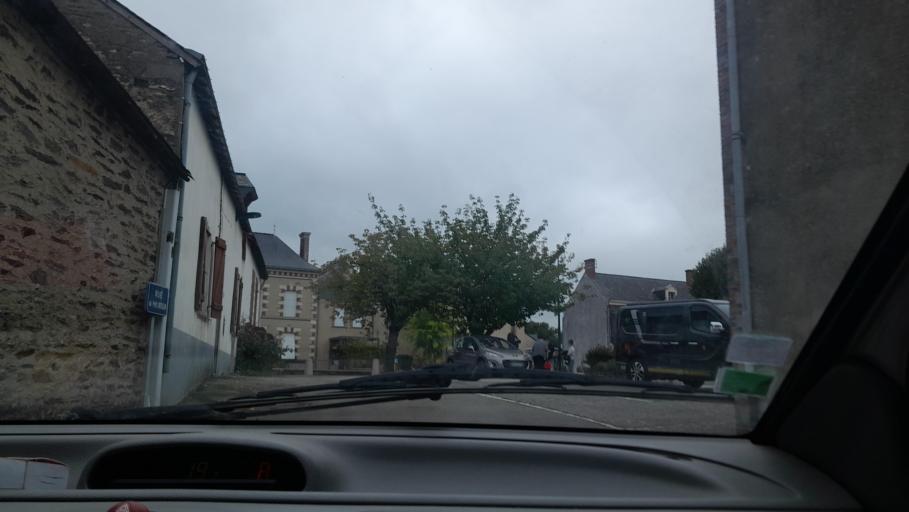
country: FR
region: Pays de la Loire
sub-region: Departement de Maine-et-Loire
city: Pouance
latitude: 47.6790
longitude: -1.1849
